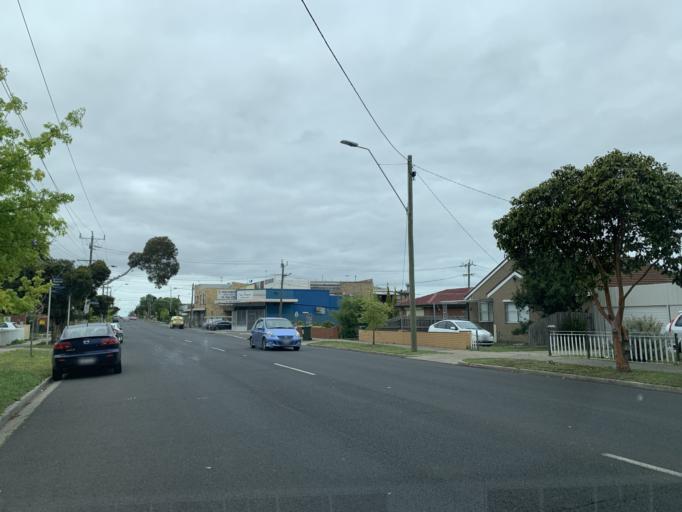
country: AU
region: Victoria
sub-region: Brimbank
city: St Albans
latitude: -37.7433
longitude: 144.7920
